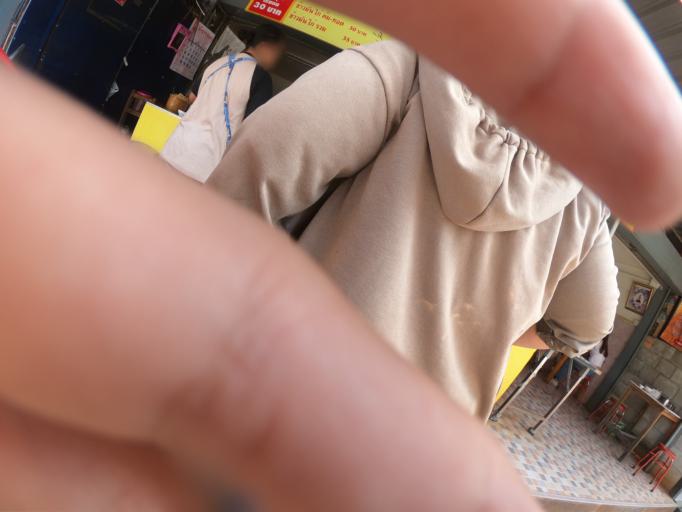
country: TH
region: Chiang Mai
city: Chiang Mai
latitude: 18.8041
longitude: 98.9918
